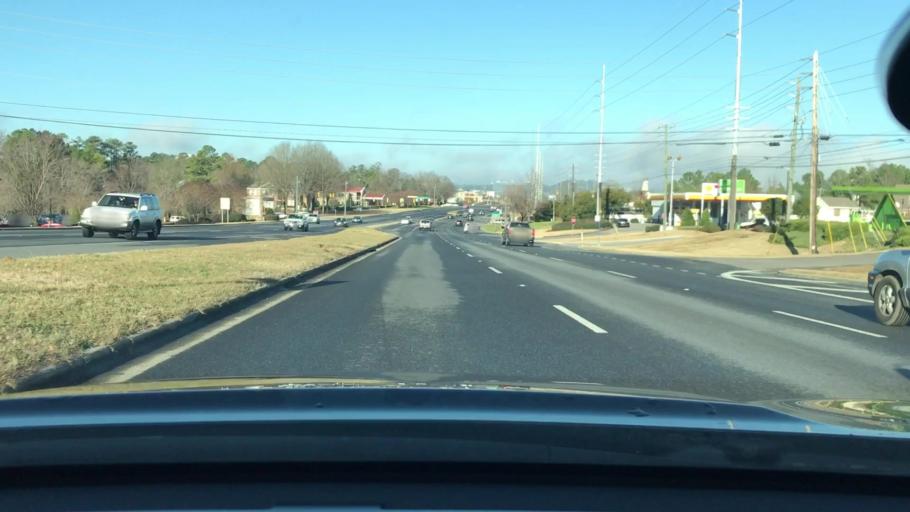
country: US
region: Alabama
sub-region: Shelby County
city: Lake Purdy
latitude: 33.4219
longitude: -86.6981
